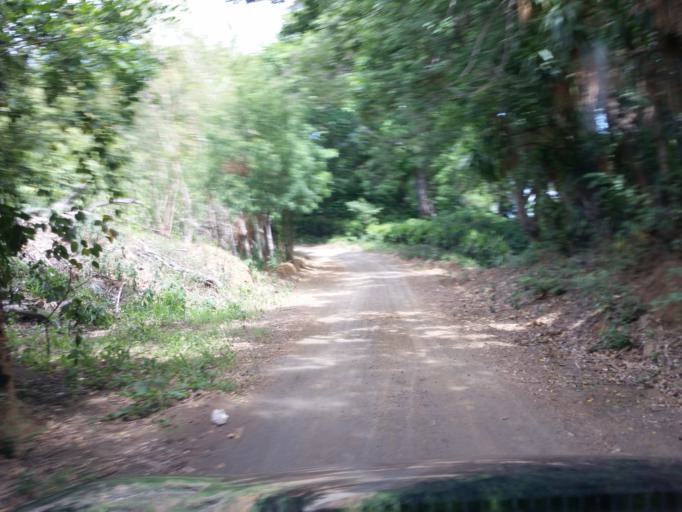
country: NI
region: Managua
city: El Crucero
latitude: 12.0062
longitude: -86.3499
